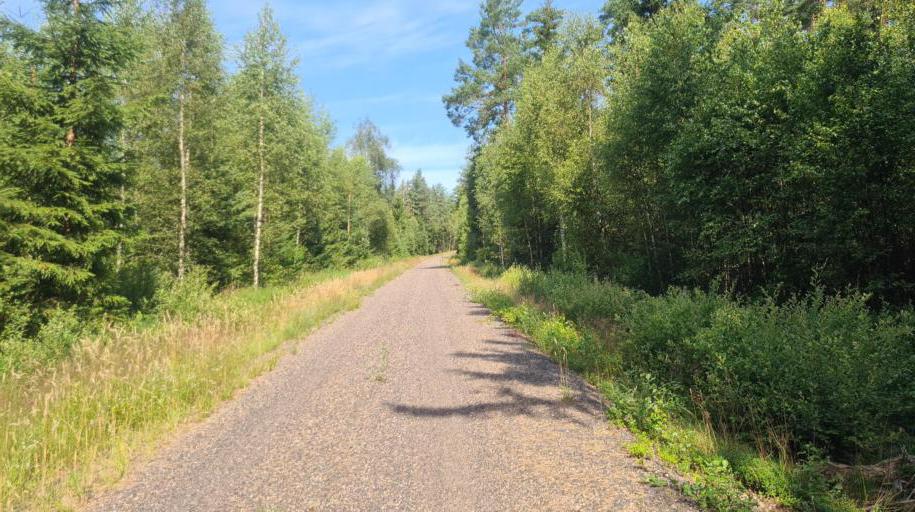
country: SE
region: Kronoberg
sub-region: Ljungby Kommun
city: Lagan
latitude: 56.9548
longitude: 13.9588
